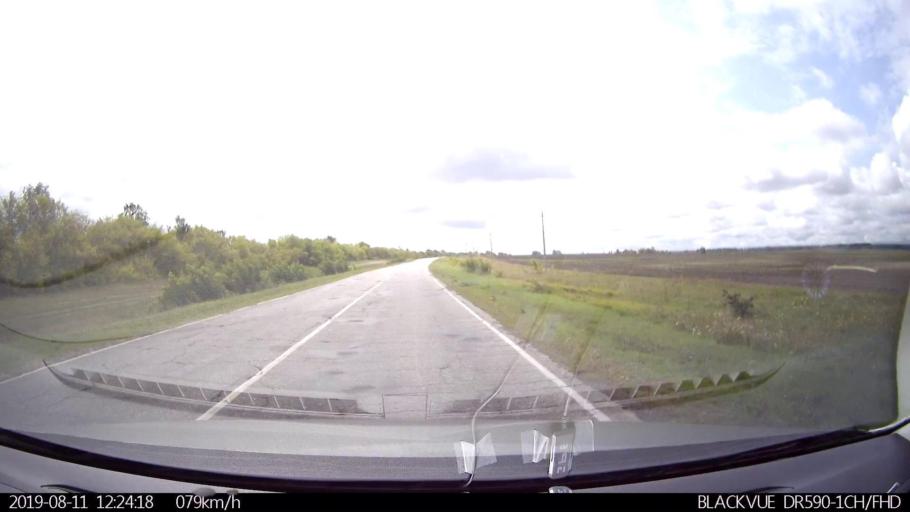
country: RU
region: Ulyanovsk
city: Ignatovka
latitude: 53.8848
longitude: 47.9494
